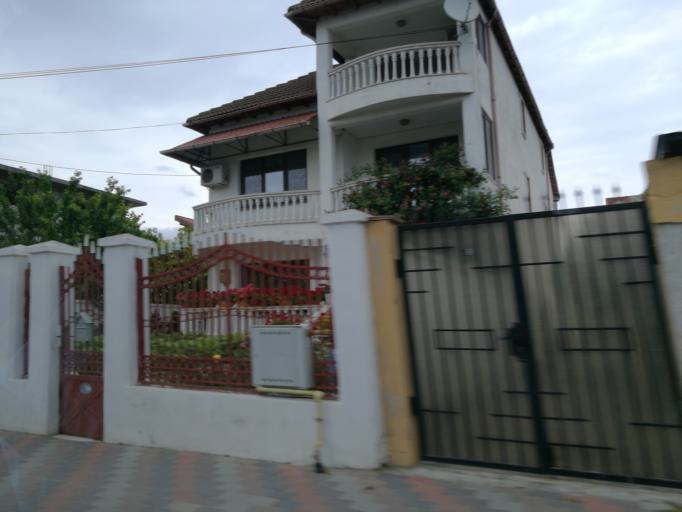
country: RO
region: Constanta
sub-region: Municipiul Mangalia
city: Mangalia
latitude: 43.8184
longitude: 28.5747
